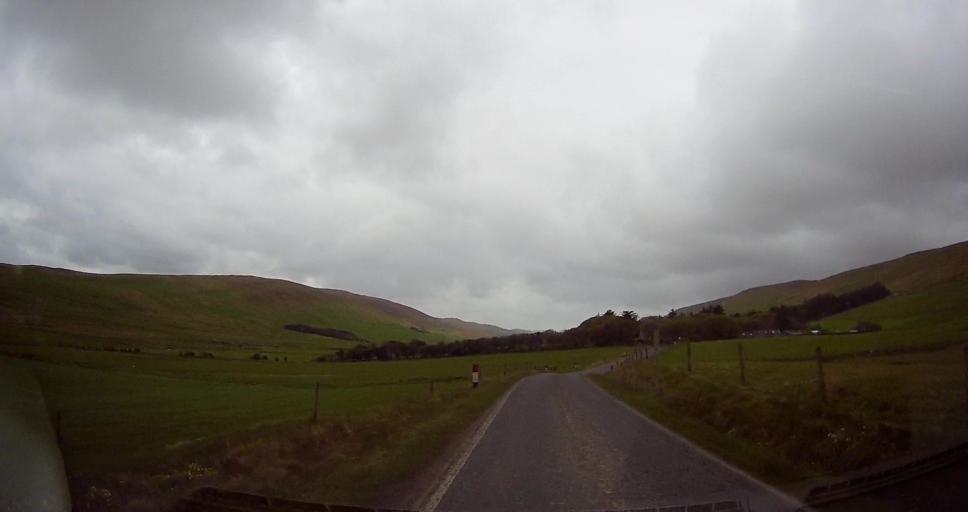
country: GB
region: Scotland
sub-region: Shetland Islands
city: Lerwick
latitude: 60.2742
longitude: -1.2845
